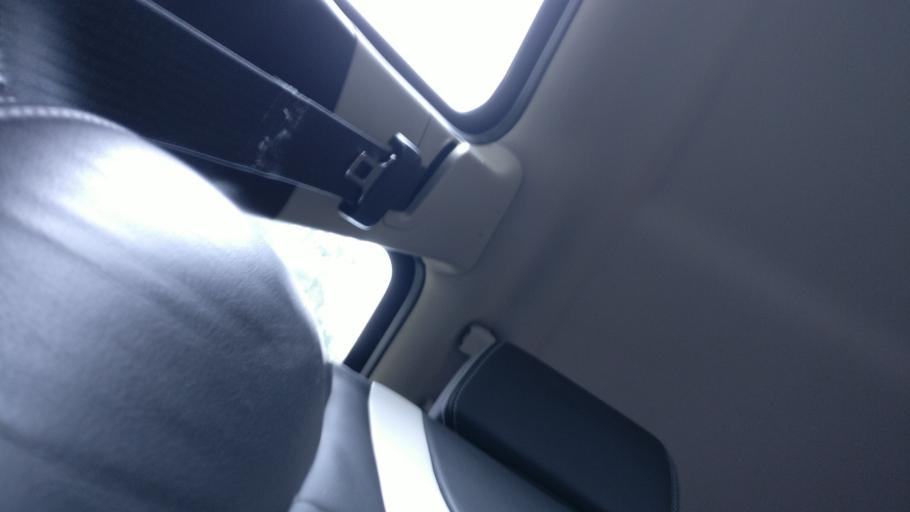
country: US
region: Oklahoma
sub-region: McClain County
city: Goldsby
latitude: 35.1895
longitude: -97.5315
